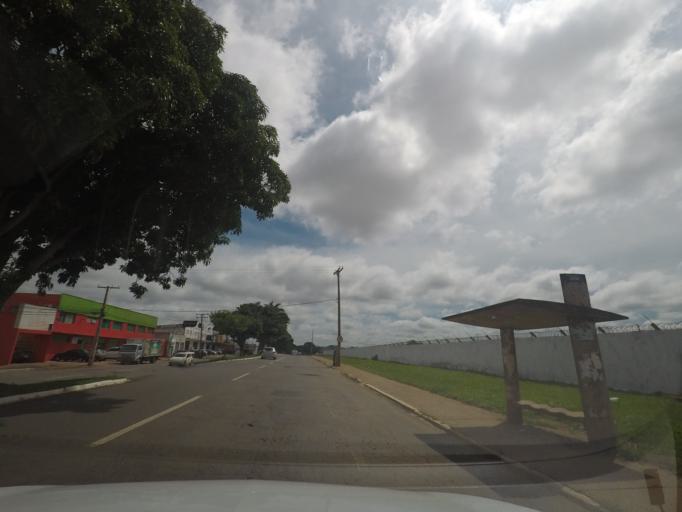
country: BR
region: Goias
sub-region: Goiania
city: Goiania
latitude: -16.6278
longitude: -49.2331
